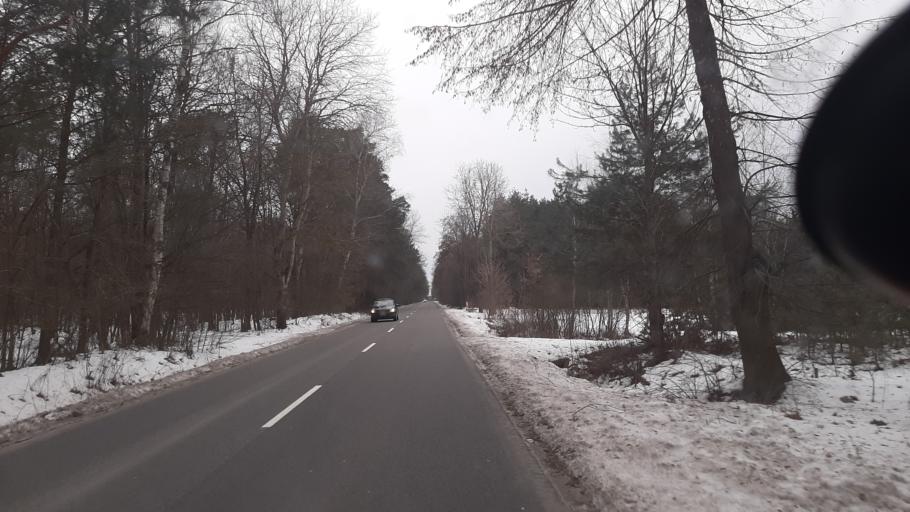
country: PL
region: Lublin Voivodeship
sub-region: Powiat lubartowski
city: Kamionka
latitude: 51.4974
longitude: 22.4133
